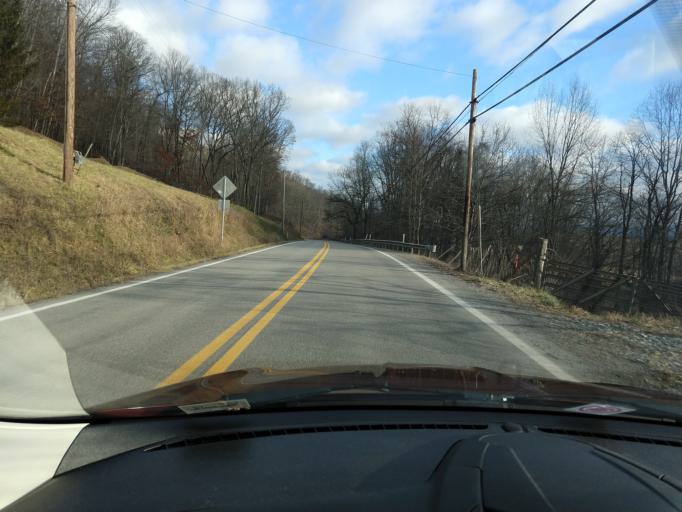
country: US
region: West Virginia
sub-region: Randolph County
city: Elkins
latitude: 38.7455
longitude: -79.9635
